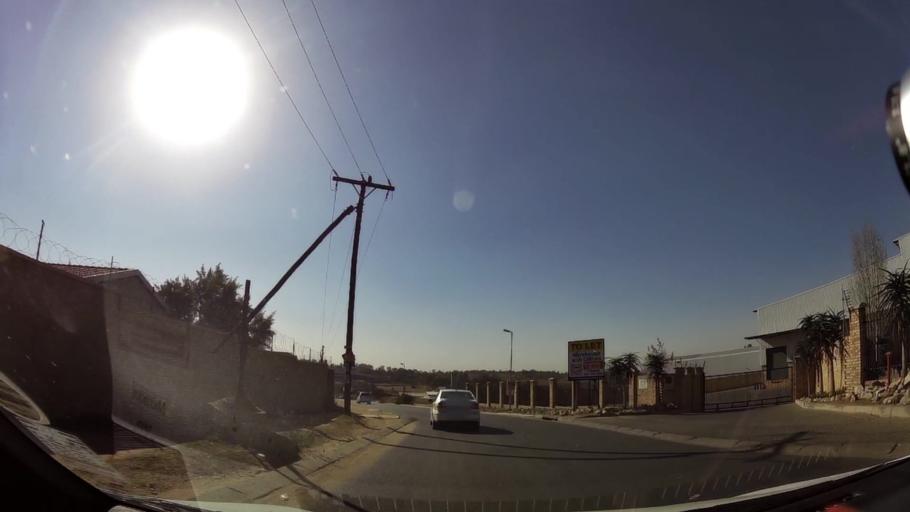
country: ZA
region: Gauteng
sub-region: City of Johannesburg Metropolitan Municipality
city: Diepsloot
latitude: -26.0127
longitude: 27.9437
